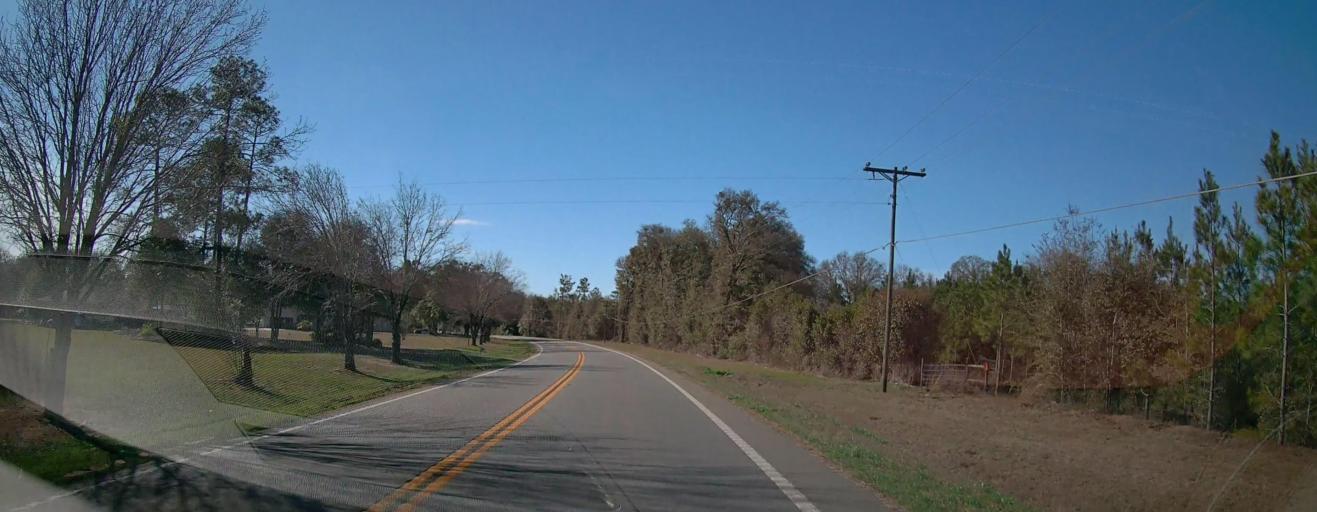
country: US
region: Georgia
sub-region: Macon County
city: Oglethorpe
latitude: 32.3288
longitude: -84.0742
